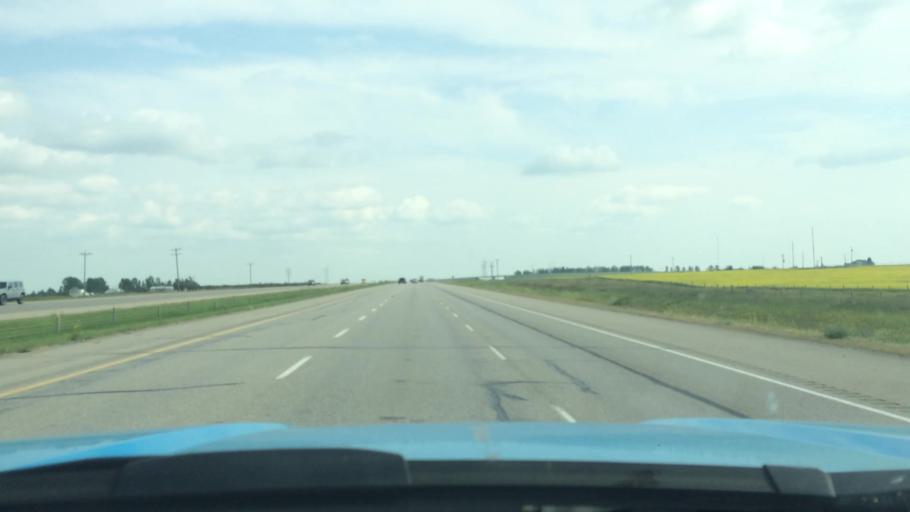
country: CA
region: Alberta
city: Crossfield
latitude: 51.4440
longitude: -114.0100
